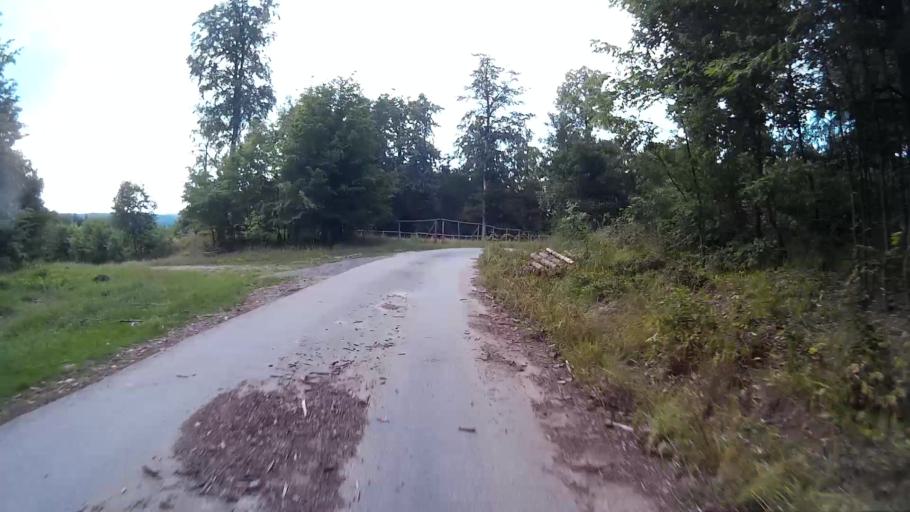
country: CZ
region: South Moravian
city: Veverska Bityska
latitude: 49.2233
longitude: 16.4534
